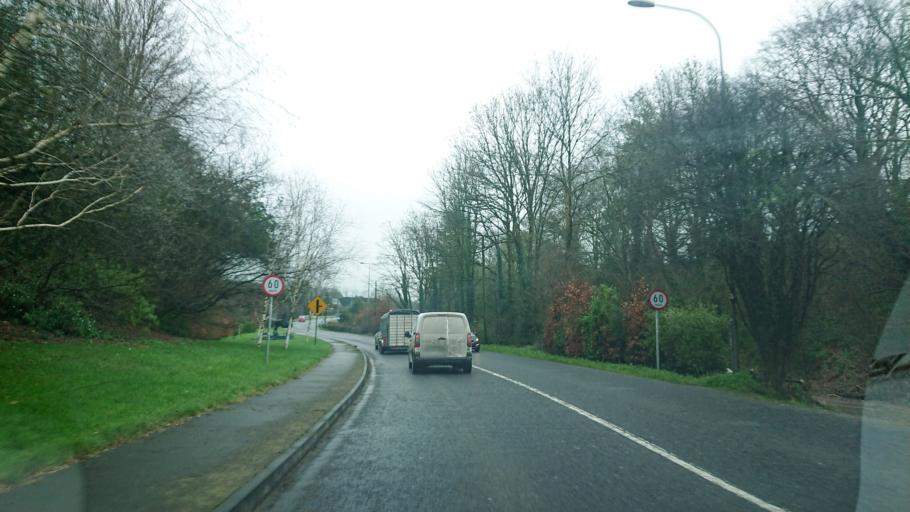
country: IE
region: Munster
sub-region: County Cork
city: Bandon
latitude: 51.7647
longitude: -8.6534
